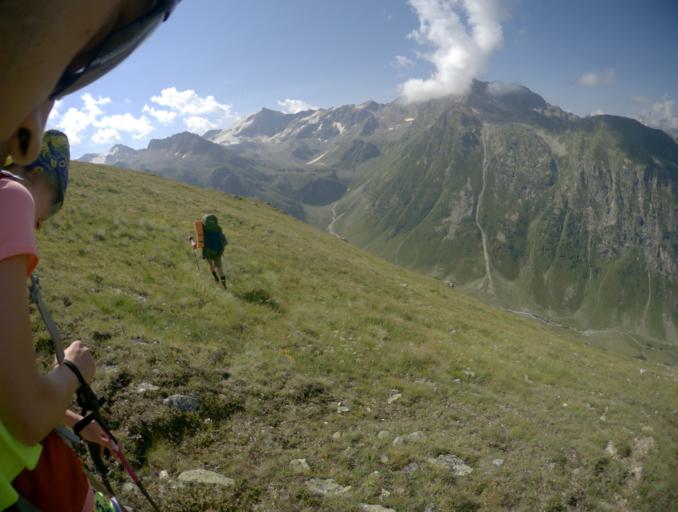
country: RU
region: Karachayevo-Cherkesiya
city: Uchkulan
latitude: 43.3016
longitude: 42.0601
